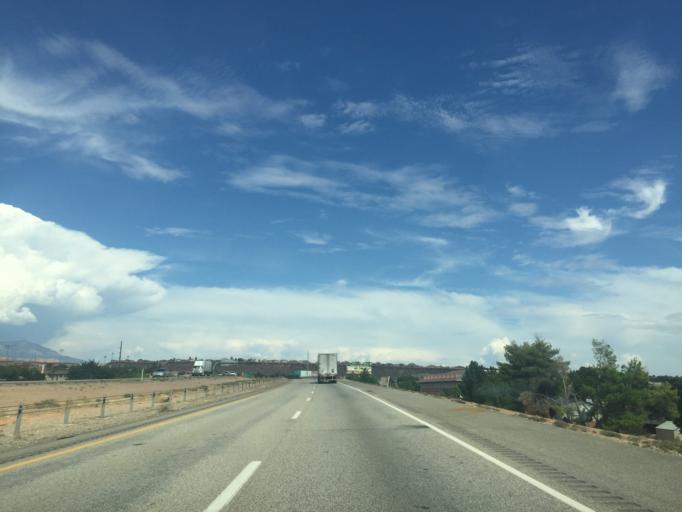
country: US
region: Utah
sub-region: Washington County
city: Saint George
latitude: 37.0946
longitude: -113.5677
